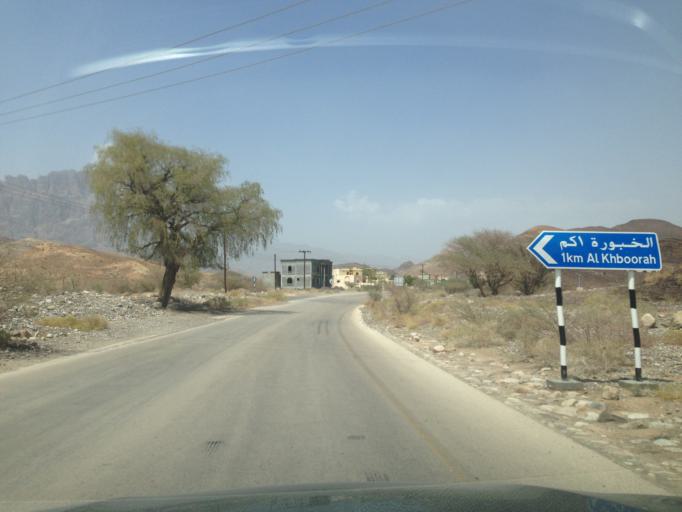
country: OM
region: Muhafazat ad Dakhiliyah
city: Bahla'
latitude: 23.2029
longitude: 56.9449
